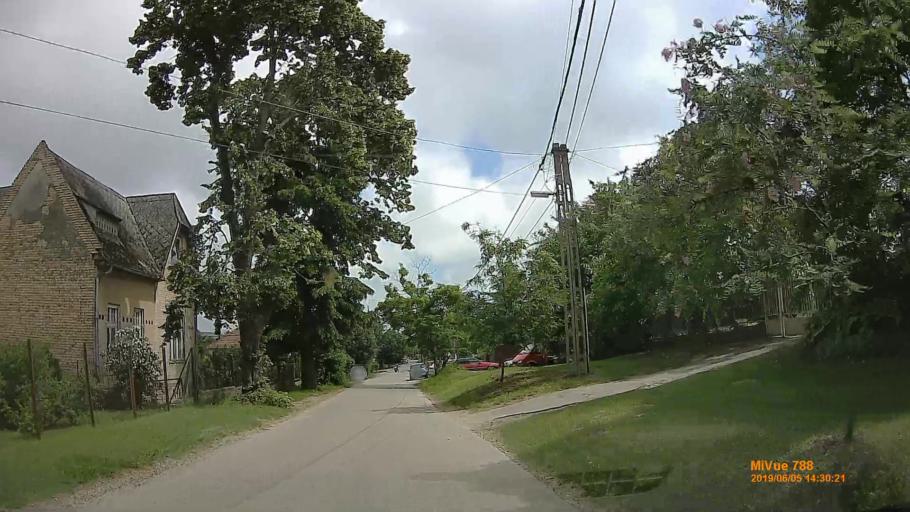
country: HU
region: Pest
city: Kistarcsa
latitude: 47.5622
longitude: 19.2599
